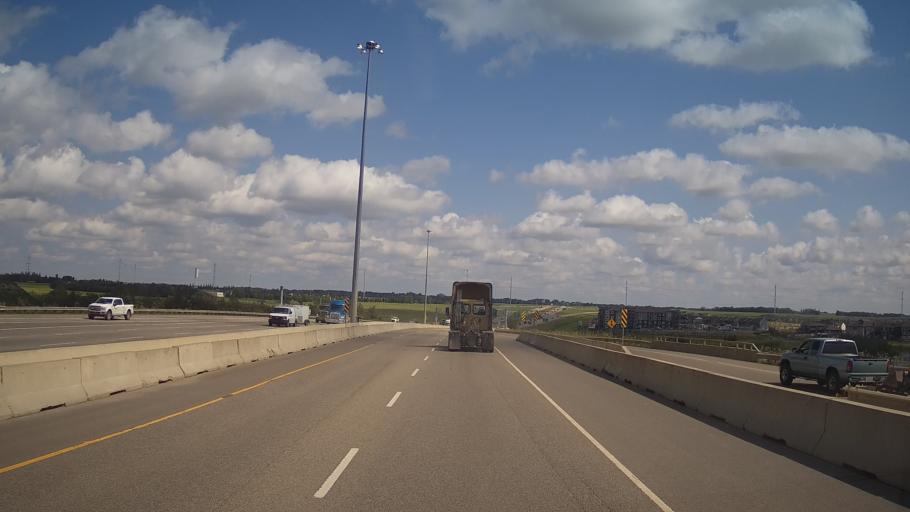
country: CA
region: Alberta
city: Sherwood Park
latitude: 53.4823
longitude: -113.3646
